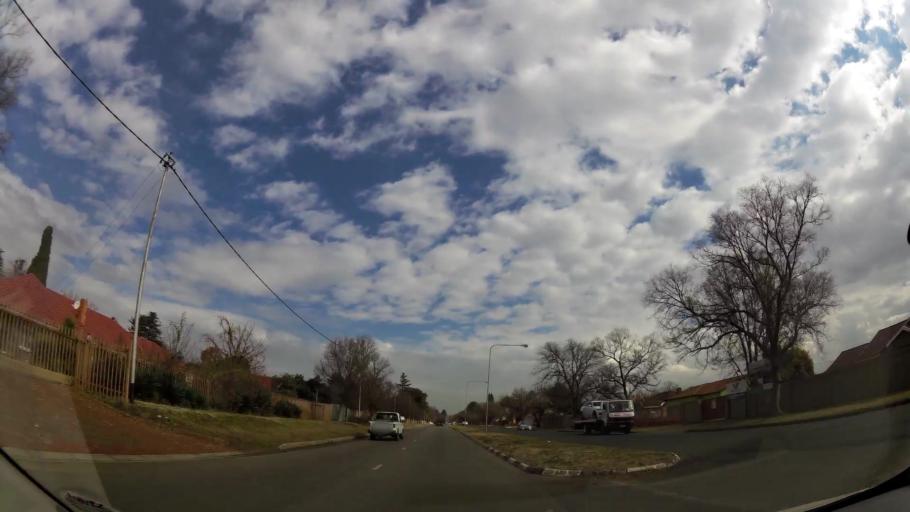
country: ZA
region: Gauteng
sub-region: Sedibeng District Municipality
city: Vereeniging
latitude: -26.6599
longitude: 27.9843
